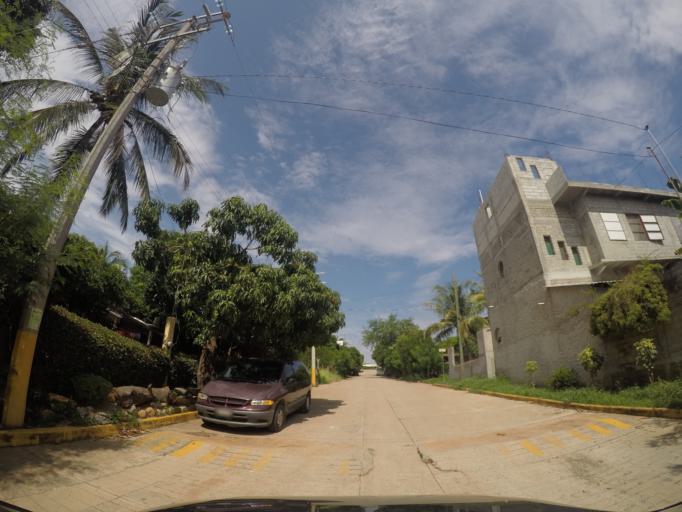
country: MX
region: Oaxaca
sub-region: Santa Maria Colotepec
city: Brisas de Zicatela
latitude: 15.8367
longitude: -97.0403
